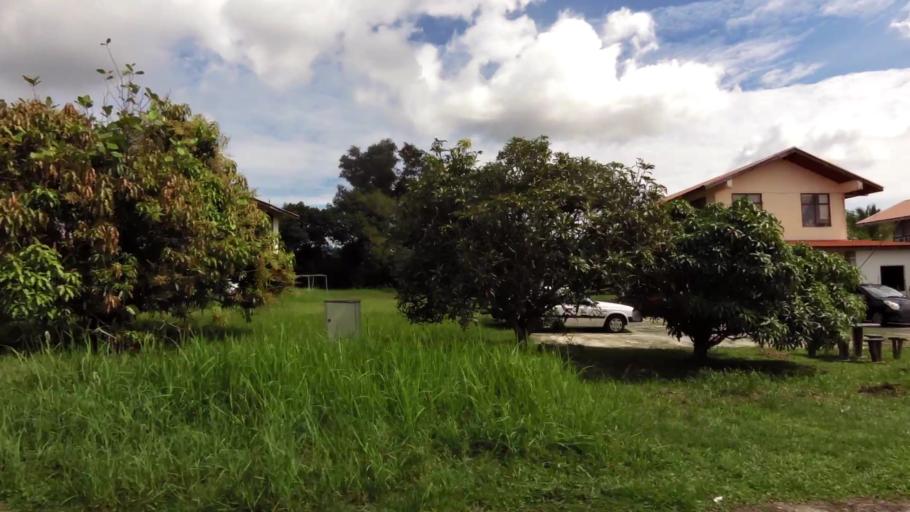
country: BN
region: Brunei and Muara
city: Bandar Seri Begawan
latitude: 4.9392
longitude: 114.9050
